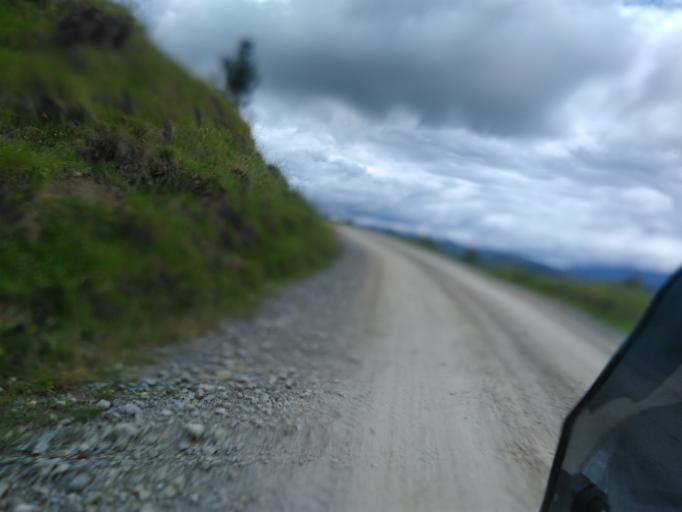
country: NZ
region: Gisborne
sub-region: Gisborne District
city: Gisborne
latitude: -38.0884
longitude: 178.0787
